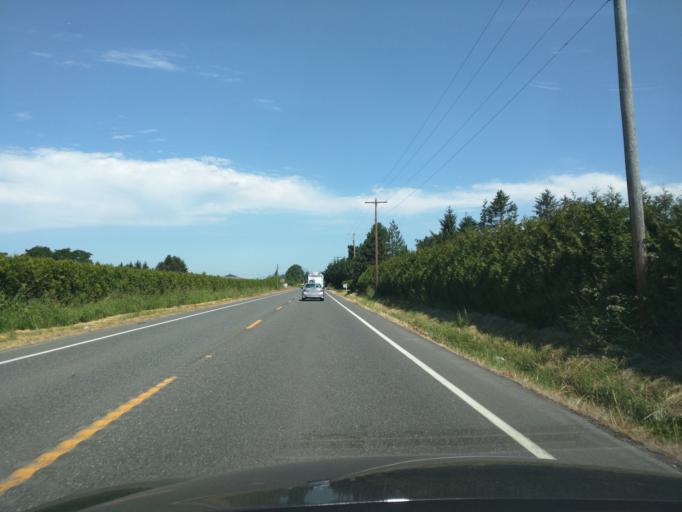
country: US
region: Washington
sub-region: Whatcom County
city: Lynden
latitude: 48.9570
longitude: -122.4852
